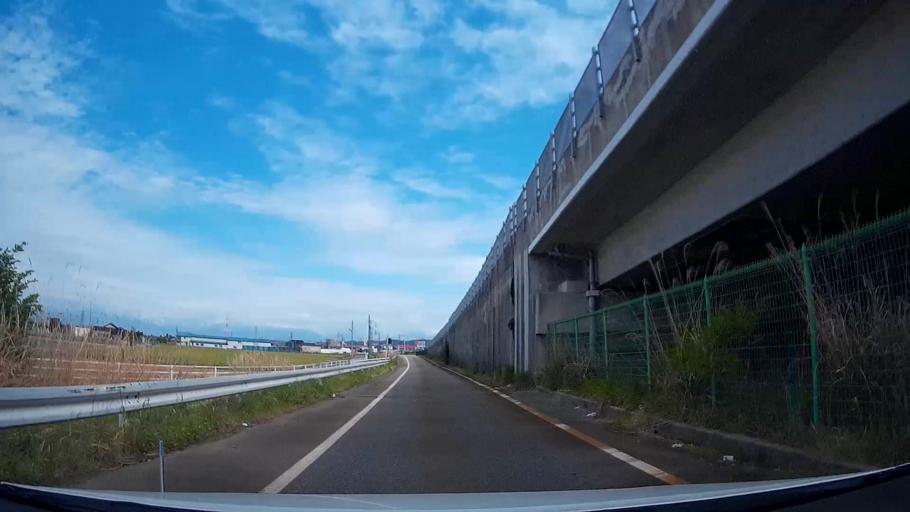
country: JP
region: Toyama
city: Kuragaki-kosugi
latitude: 36.7289
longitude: 137.1247
